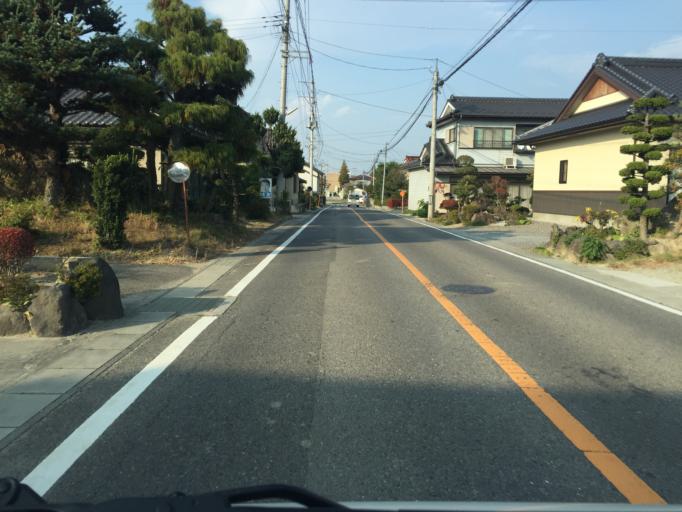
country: JP
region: Fukushima
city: Motomiya
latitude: 37.4939
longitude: 140.4014
